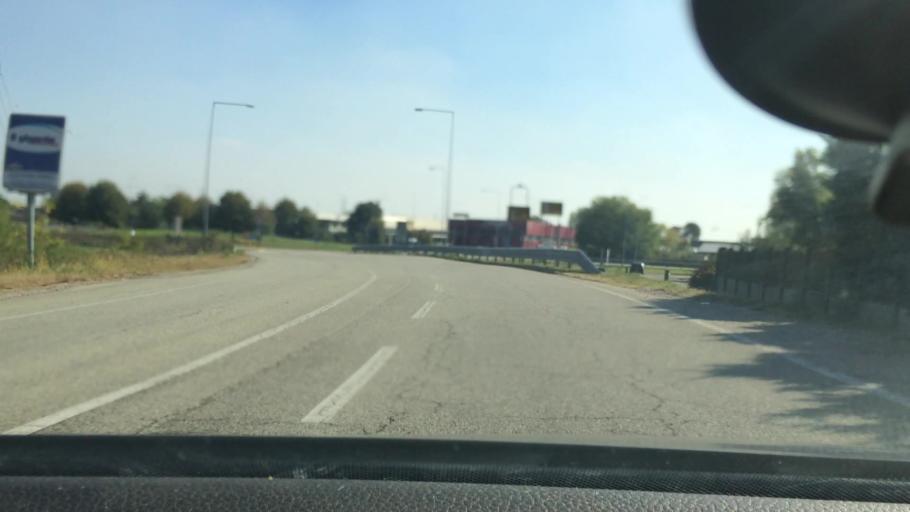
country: IT
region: Lombardy
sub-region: Citta metropolitana di Milano
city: Casate
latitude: 45.4826
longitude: 8.8308
